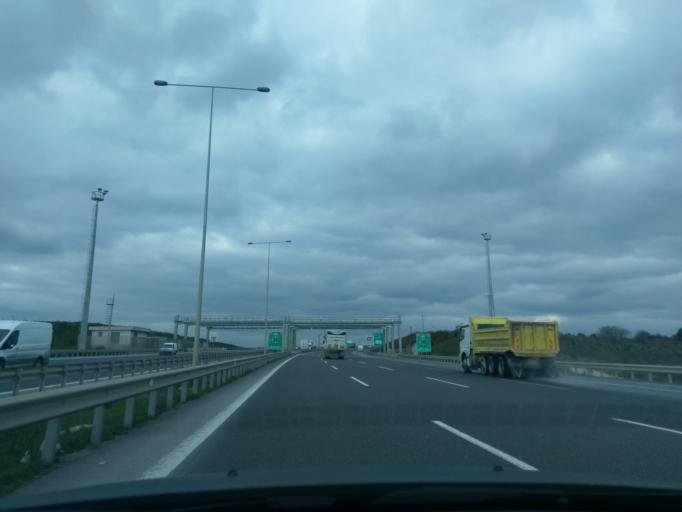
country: TR
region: Istanbul
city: Basaksehir
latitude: 41.1267
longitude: 28.8084
